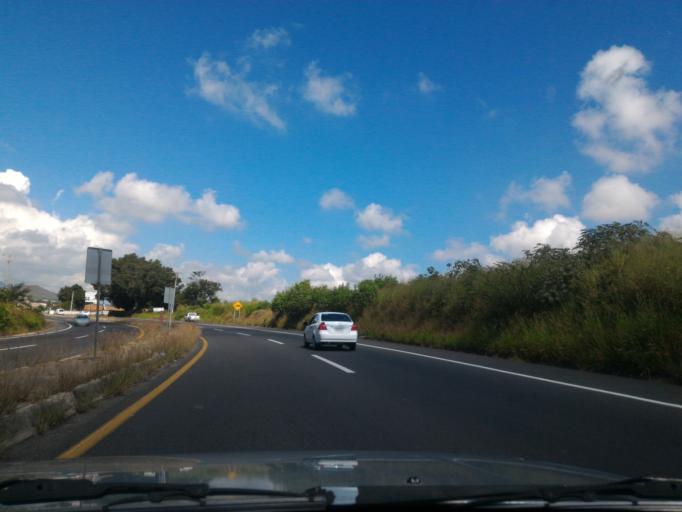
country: MX
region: Jalisco
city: Arenal
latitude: 20.7449
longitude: -103.6386
